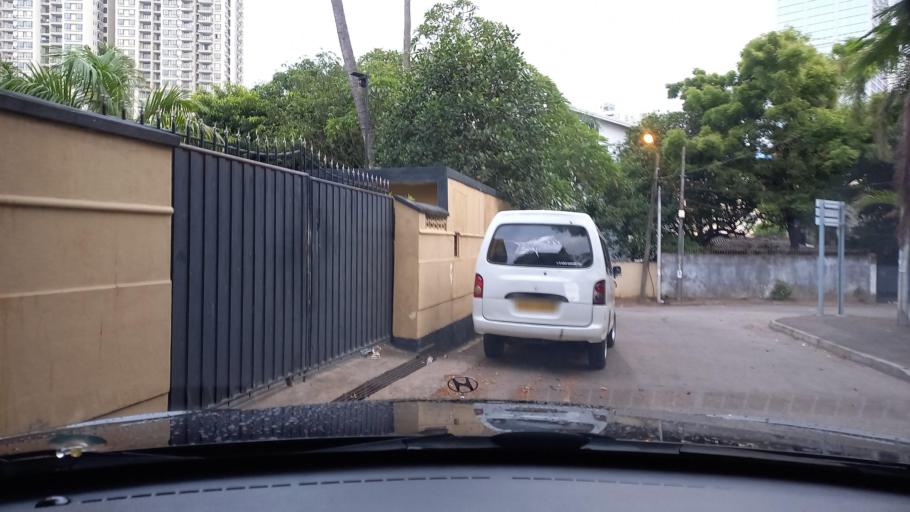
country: LK
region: Western
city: Pita Kotte
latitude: 6.8795
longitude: 79.8676
